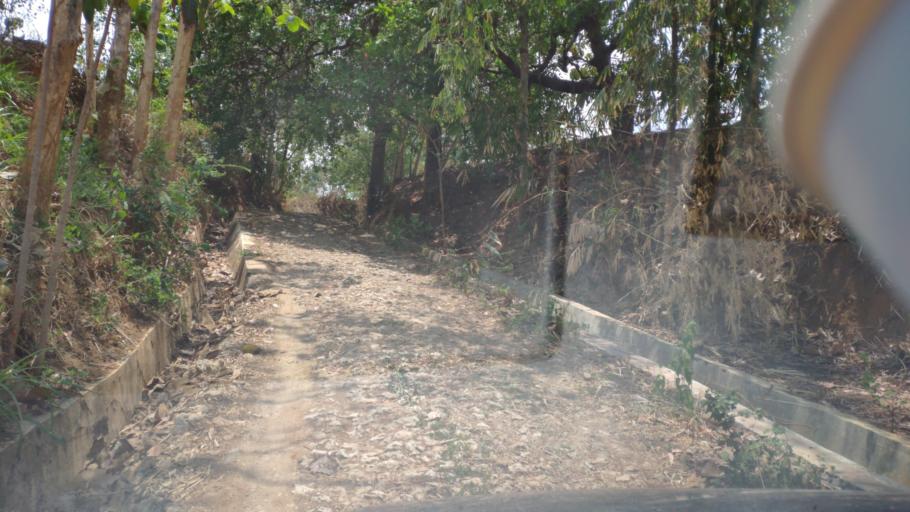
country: ID
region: Central Java
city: Ngapus
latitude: -6.9542
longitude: 111.1854
